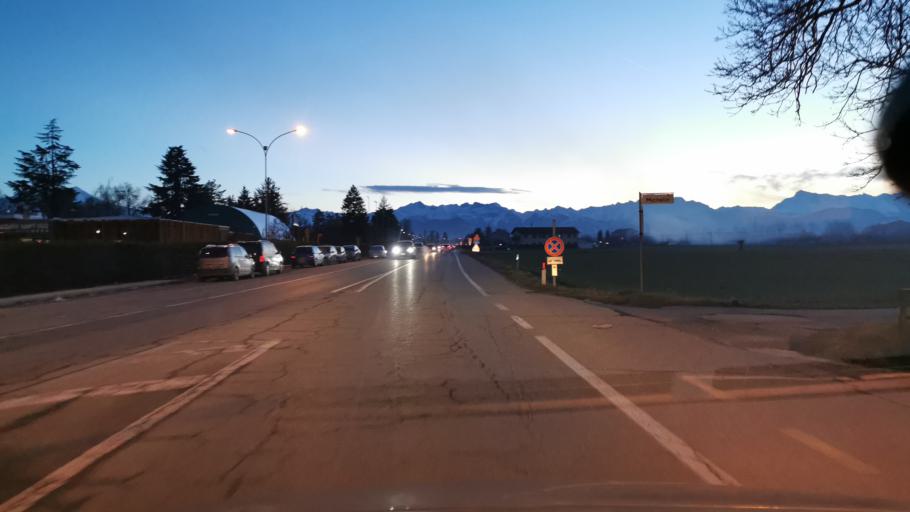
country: IT
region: Piedmont
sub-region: Provincia di Cuneo
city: Roata Rossi
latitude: 44.4401
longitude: 7.5635
